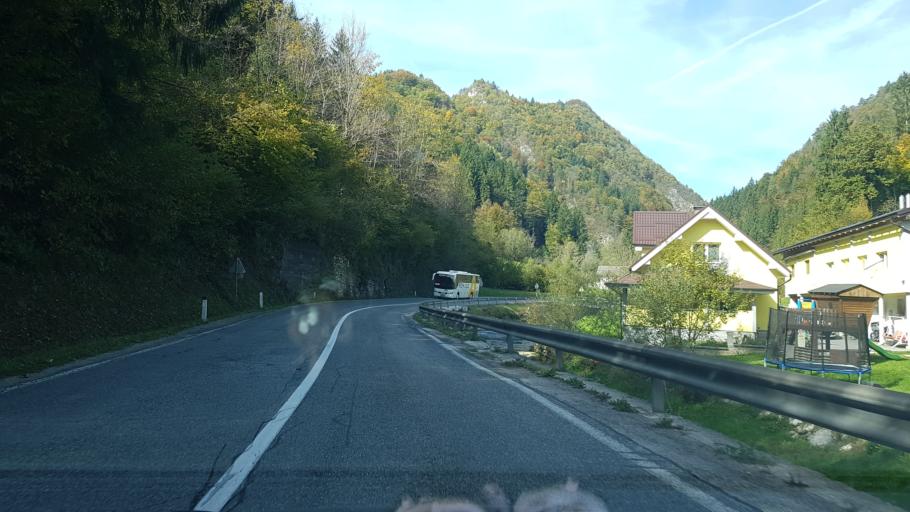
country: SI
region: Velenje
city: Velenje
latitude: 46.4096
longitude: 15.1794
